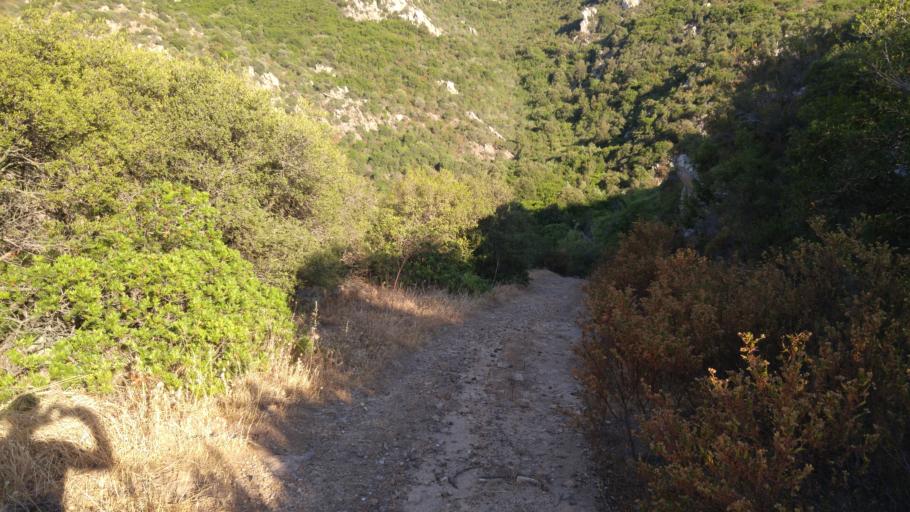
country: IT
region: Sardinia
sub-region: Provincia di Olbia-Tempio
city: San Teodoro
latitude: 40.7443
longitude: 9.6075
